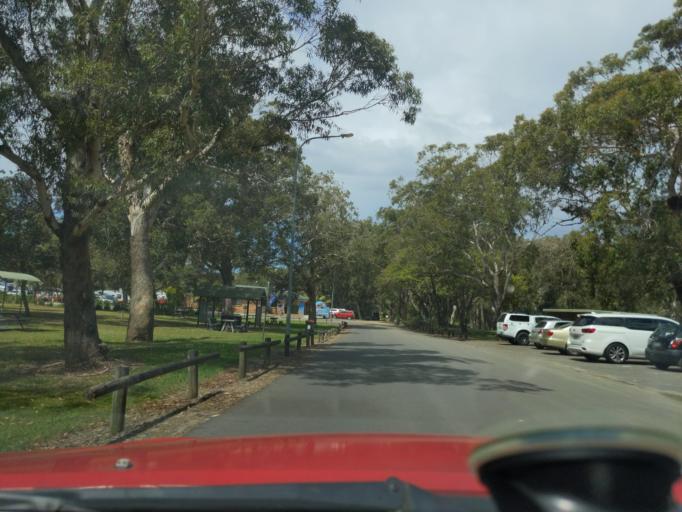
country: AU
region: New South Wales
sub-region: Great Lakes
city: Hawks Nest
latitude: -32.6780
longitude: 152.1776
